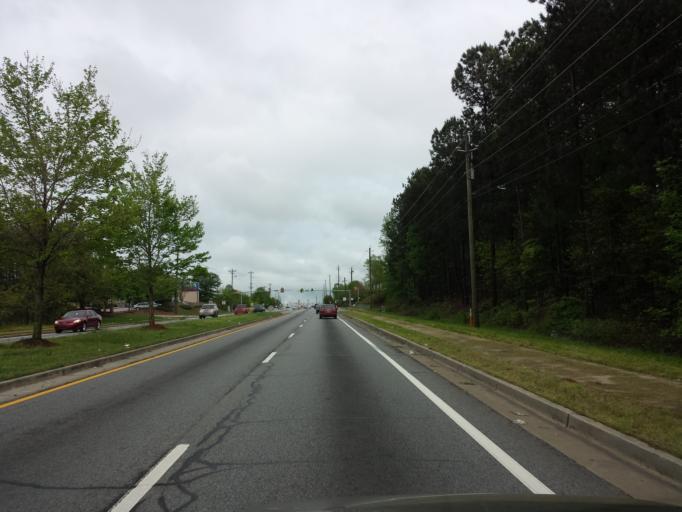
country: US
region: Georgia
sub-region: Cobb County
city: Mableton
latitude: 33.8540
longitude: -84.6107
